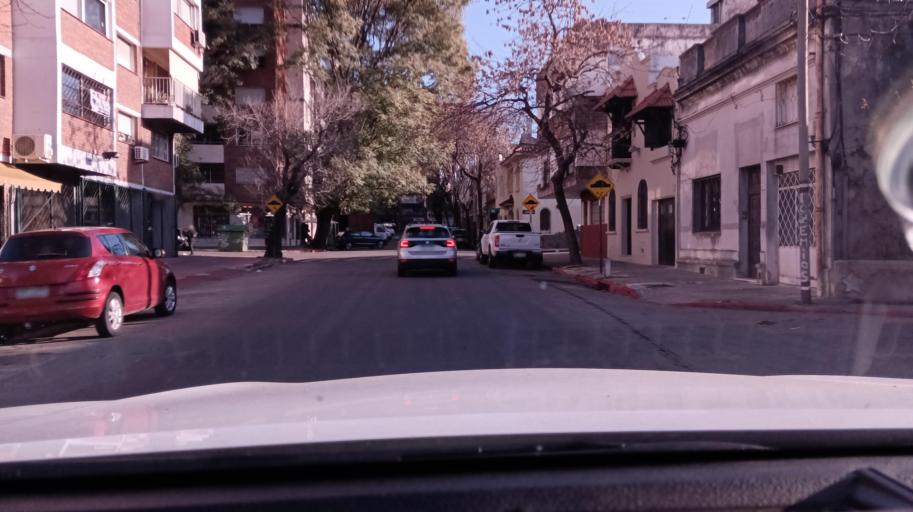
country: UY
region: Montevideo
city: Montevideo
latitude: -34.9055
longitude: -56.1496
